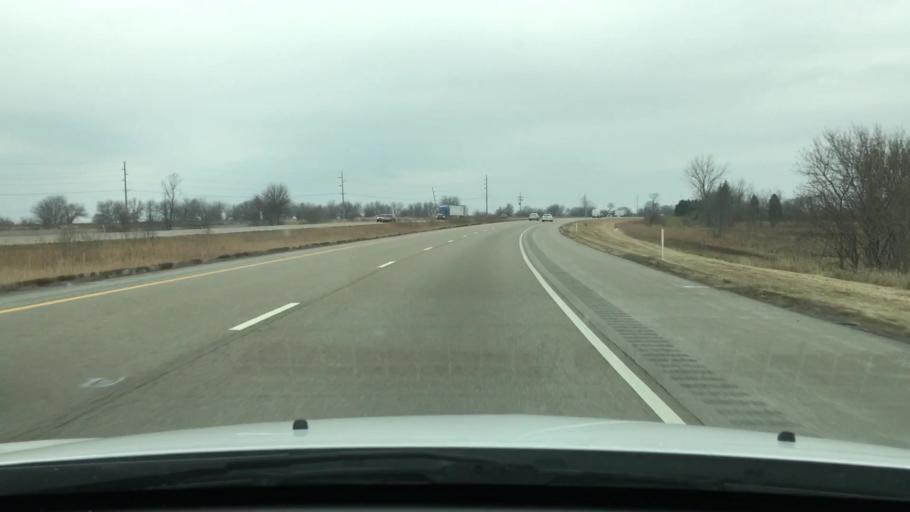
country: US
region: Illinois
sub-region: Logan County
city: Atlanta
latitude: 40.2741
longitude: -89.2121
